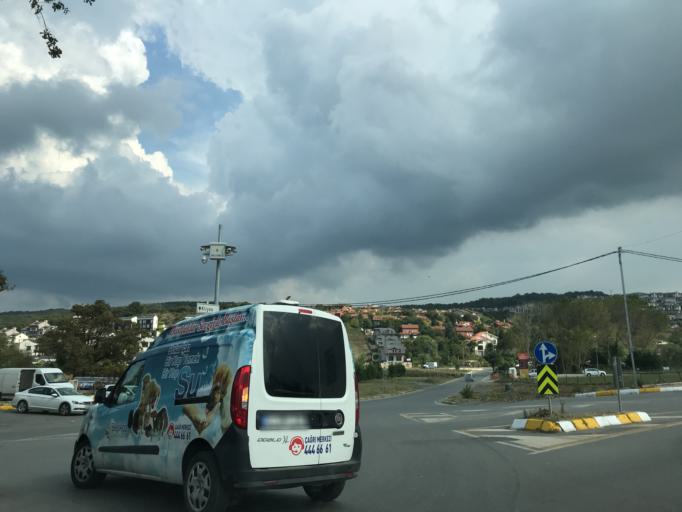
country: TR
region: Istanbul
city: Arikoey
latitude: 41.2201
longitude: 29.0324
